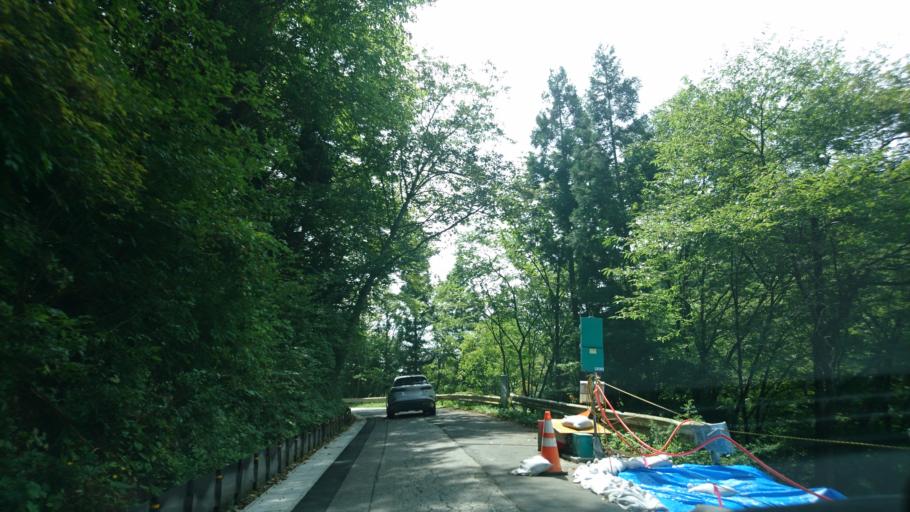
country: JP
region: Iwate
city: Ofunato
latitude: 38.9323
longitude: 141.5929
